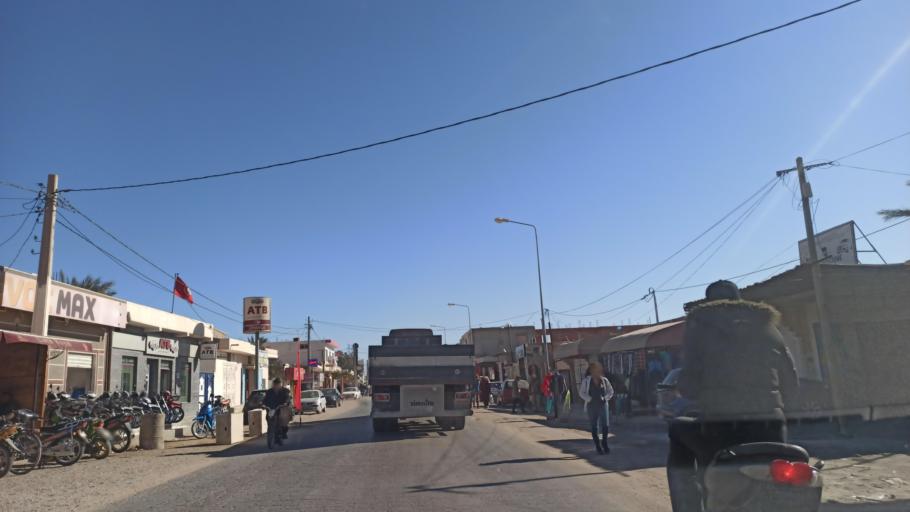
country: TN
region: Gafsa
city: Al Metlaoui
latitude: 34.3161
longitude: 8.3988
